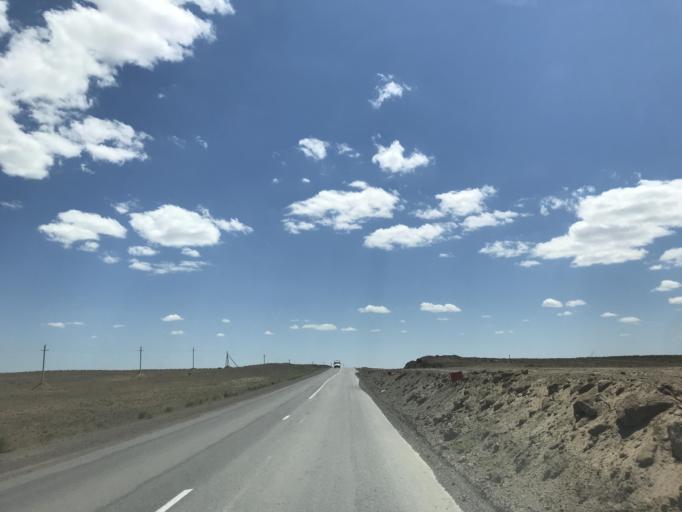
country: KZ
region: Almaty Oblysy
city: Ulken
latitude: 44.9735
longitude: 74.0165
